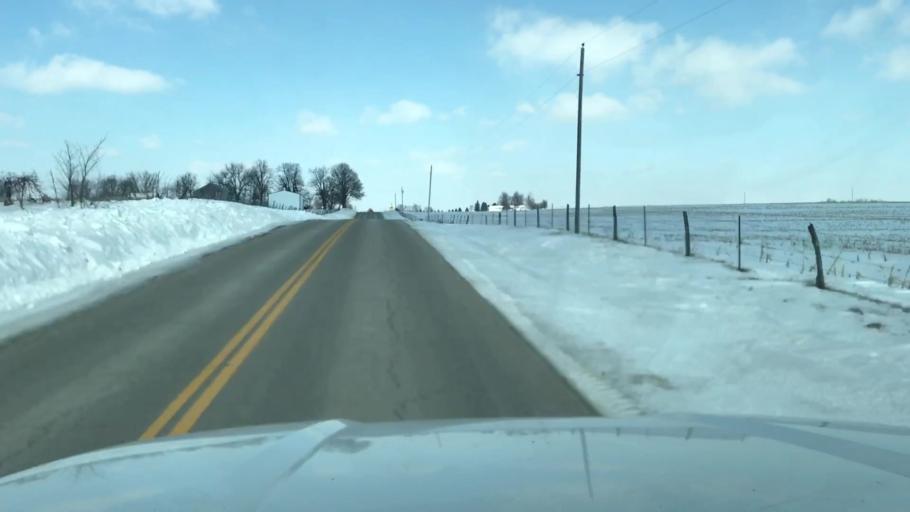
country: US
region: Missouri
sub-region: Nodaway County
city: Maryville
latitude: 40.3544
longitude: -94.7221
